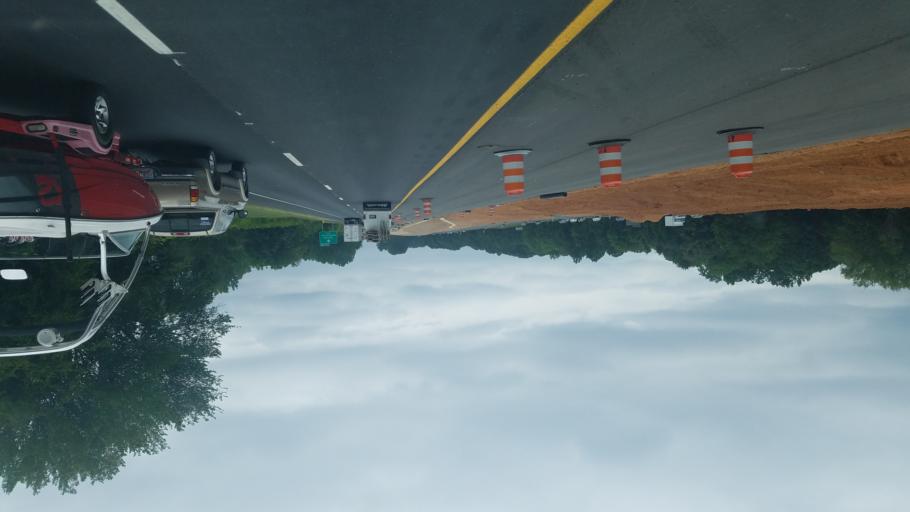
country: US
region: North Carolina
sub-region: Mecklenburg County
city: Huntersville
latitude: 35.4242
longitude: -80.8633
